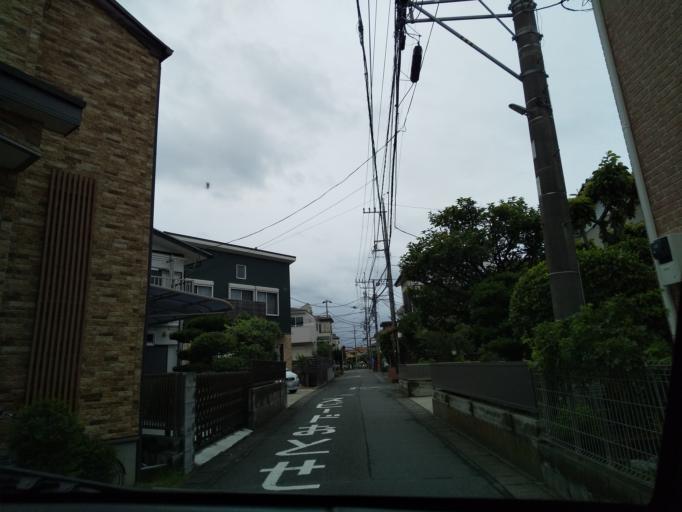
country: JP
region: Kanagawa
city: Minami-rinkan
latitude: 35.4349
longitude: 139.4439
